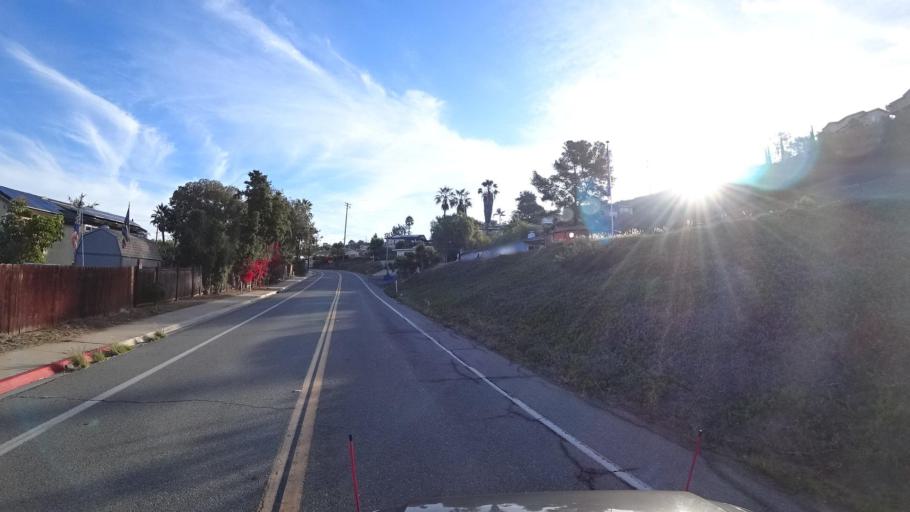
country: US
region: California
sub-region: San Diego County
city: Spring Valley
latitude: 32.7278
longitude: -116.9982
